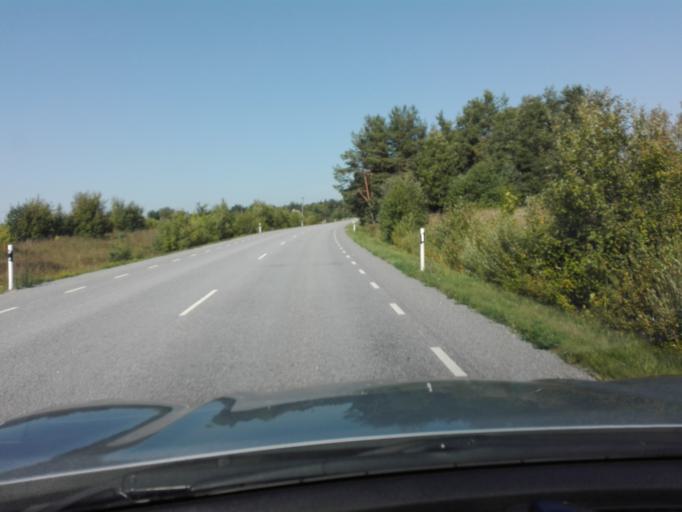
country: EE
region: Raplamaa
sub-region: Rapla vald
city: Rapla
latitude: 58.9977
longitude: 24.7691
